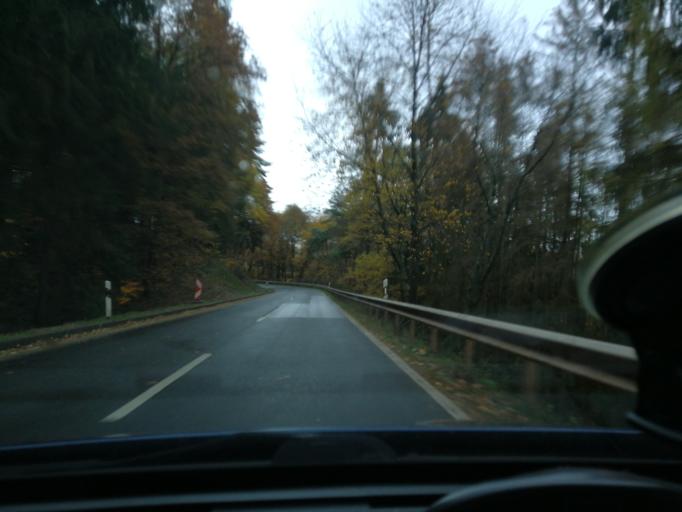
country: DE
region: Rheinland-Pfalz
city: Klausen
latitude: 49.8962
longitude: 6.8929
